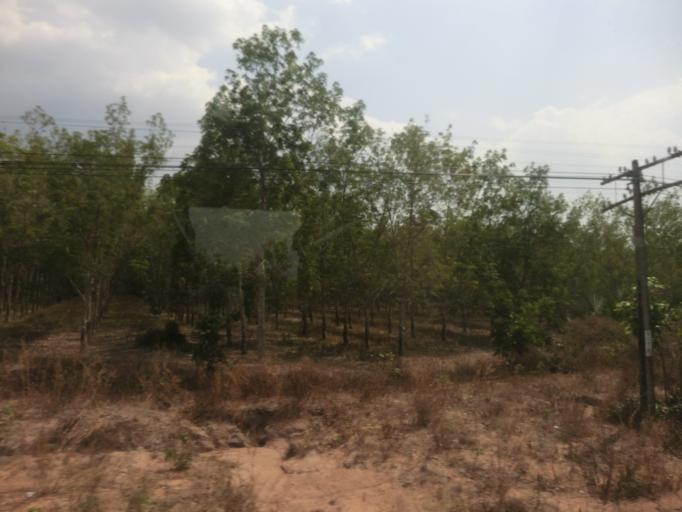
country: VN
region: Binh Thuan
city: Tanh Linh
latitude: 10.9856
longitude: 107.5769
